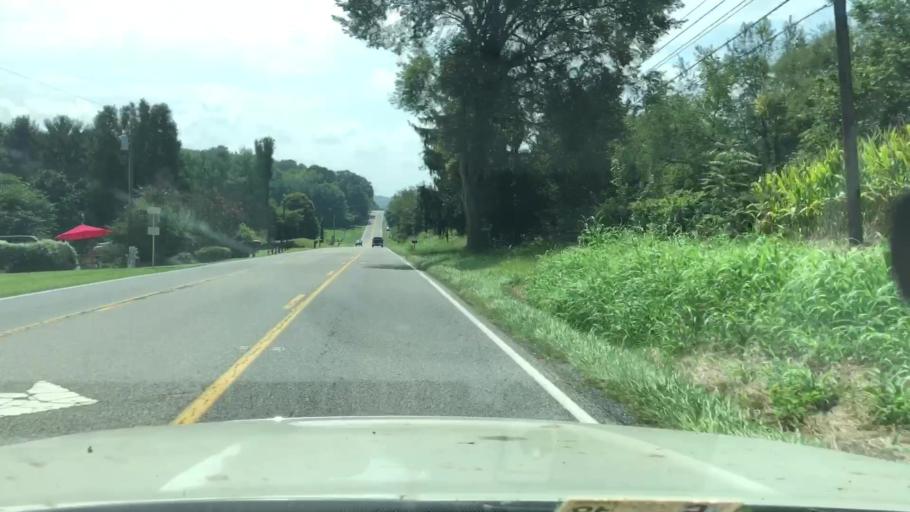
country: US
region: Virginia
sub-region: Augusta County
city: Weyers Cave
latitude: 38.3202
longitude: -78.9368
